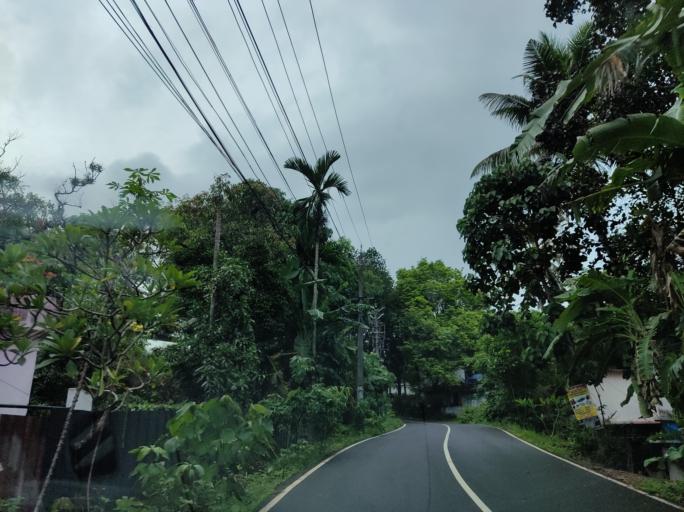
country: IN
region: Kerala
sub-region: Alappuzha
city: Mavelikara
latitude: 9.2328
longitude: 76.5618
